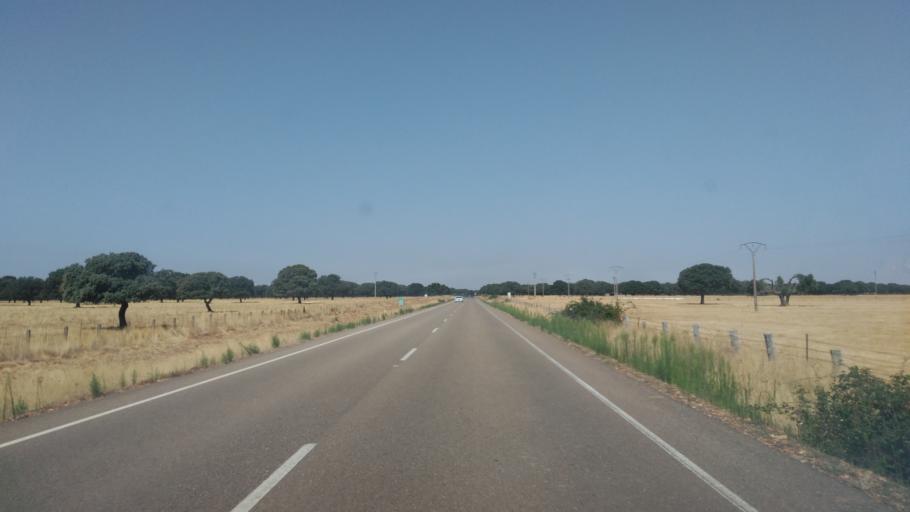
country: ES
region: Castille and Leon
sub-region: Provincia de Salamanca
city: Tamames
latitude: 40.6771
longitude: -6.1259
